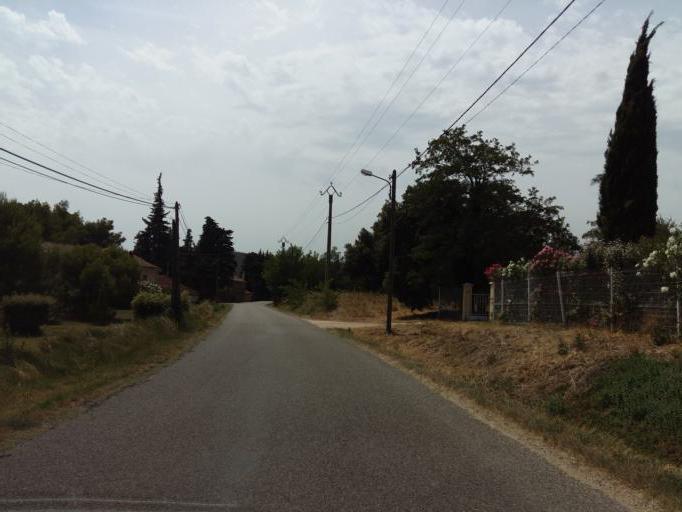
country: FR
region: Provence-Alpes-Cote d'Azur
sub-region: Departement du Vaucluse
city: Piolenc
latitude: 44.1973
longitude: 4.7827
